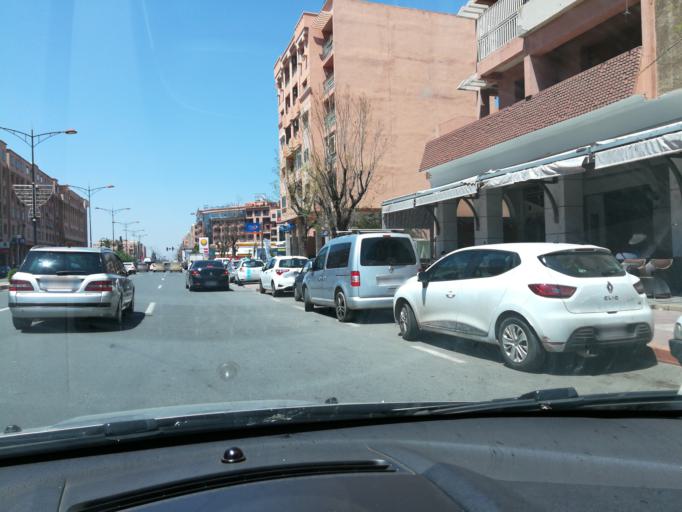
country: MA
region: Marrakech-Tensift-Al Haouz
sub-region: Marrakech
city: Marrakesh
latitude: 31.6360
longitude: -8.0173
